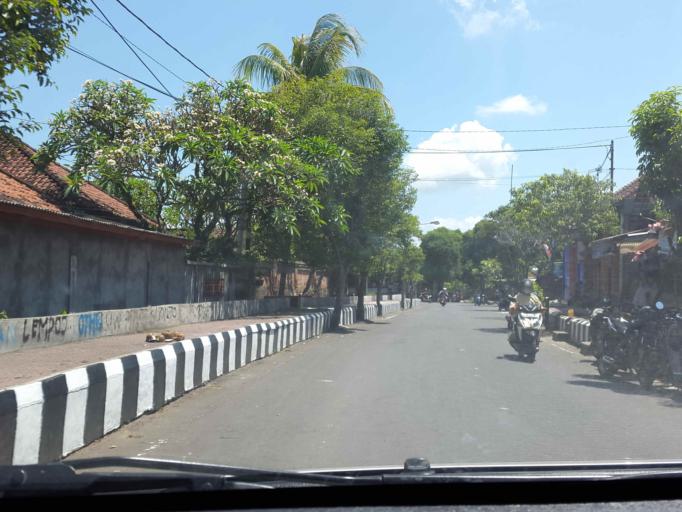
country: ID
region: Bali
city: Semarapura
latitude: -8.5395
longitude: 115.4022
